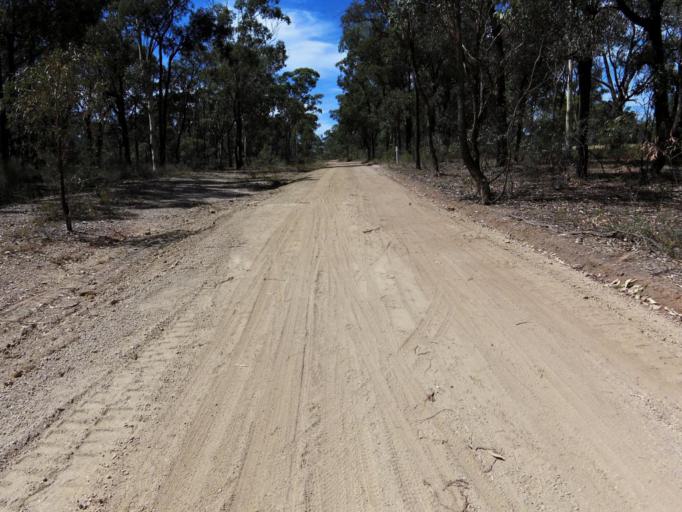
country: AU
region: Victoria
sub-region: Greater Bendigo
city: White Hills
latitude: -36.7568
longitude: 144.3302
